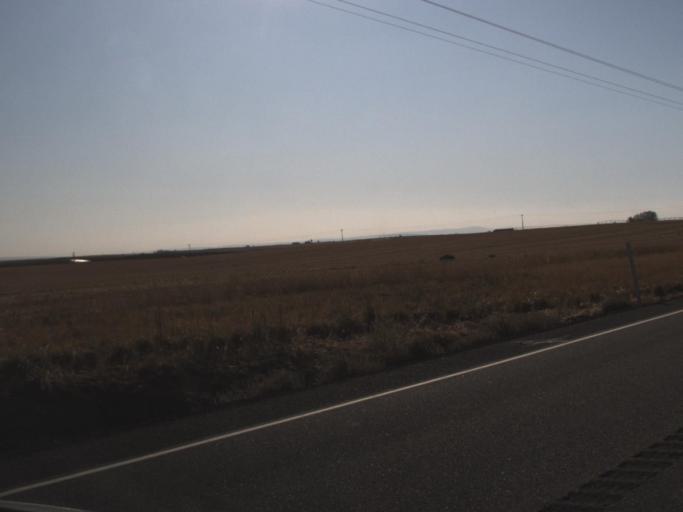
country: US
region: Washington
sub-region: Walla Walla County
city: Garrett
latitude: 46.2963
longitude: -118.6214
